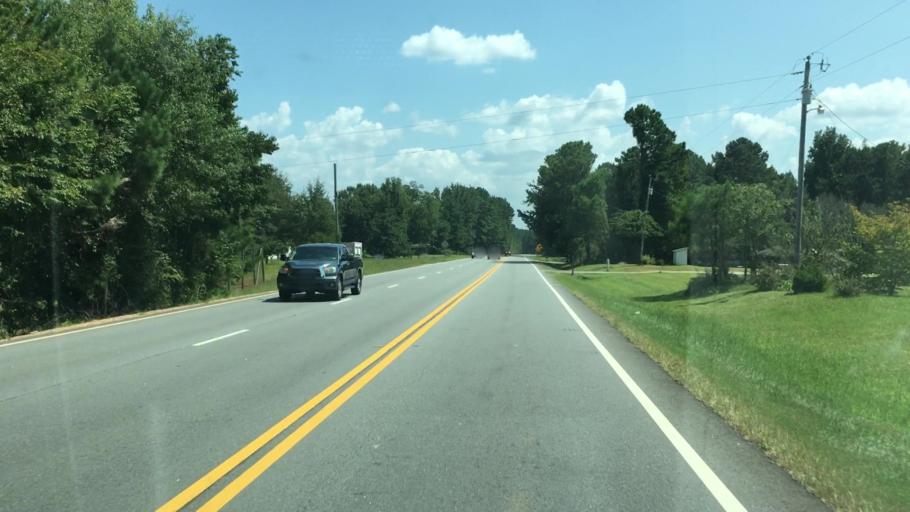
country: US
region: Georgia
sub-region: Oconee County
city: Watkinsville
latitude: 33.7424
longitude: -83.4310
